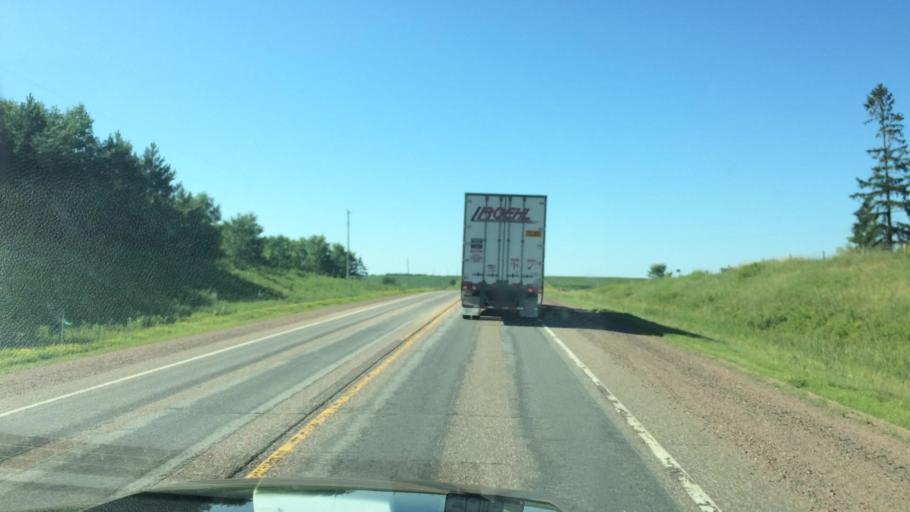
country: US
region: Wisconsin
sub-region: Marathon County
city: Athens
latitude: 44.9254
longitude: -90.0788
